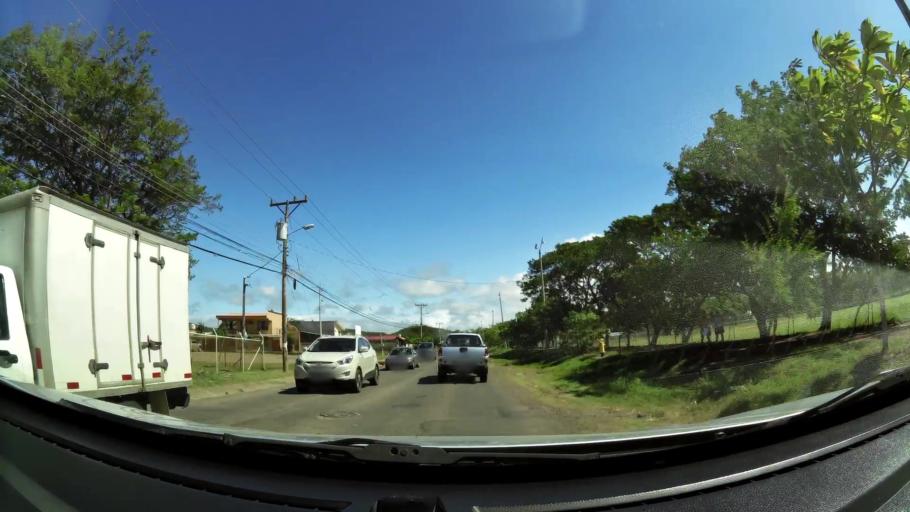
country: CR
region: Guanacaste
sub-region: Canton de Canas
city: Canas
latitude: 10.4312
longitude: -85.0878
